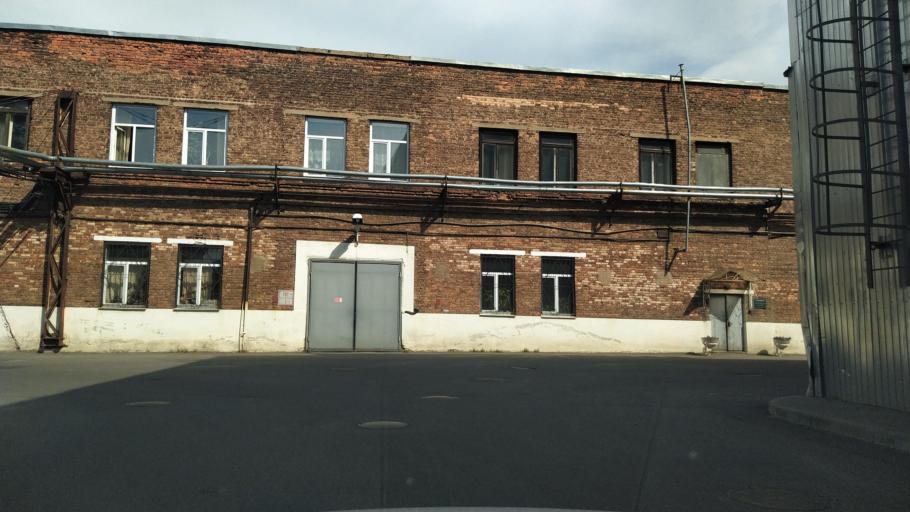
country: RU
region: Leningrad
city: Finlyandskiy
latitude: 59.9608
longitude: 30.3655
